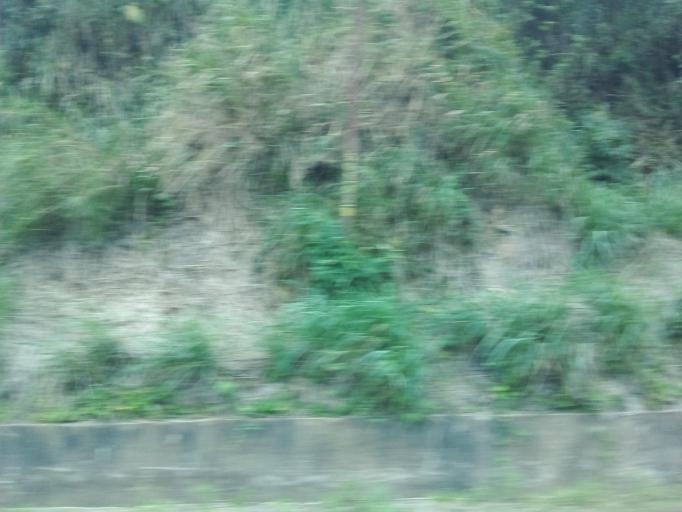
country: BR
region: Minas Gerais
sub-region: Nova Era
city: Nova Era
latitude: -19.7319
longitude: -43.0004
